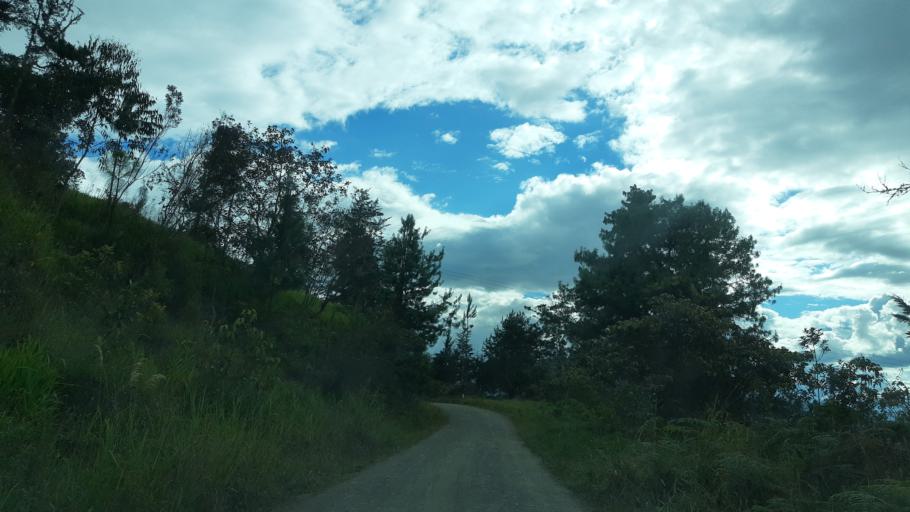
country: CO
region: Boyaca
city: Garagoa
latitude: 5.0109
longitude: -73.3395
